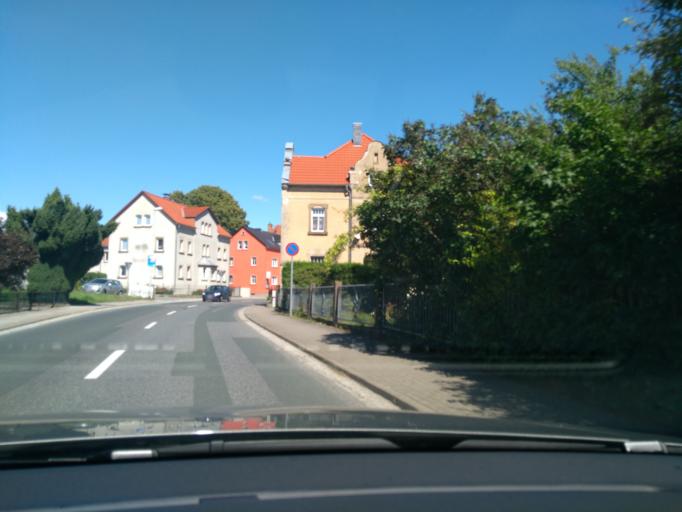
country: DE
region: Saxony
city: Hauswalde
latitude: 51.1448
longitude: 14.0534
